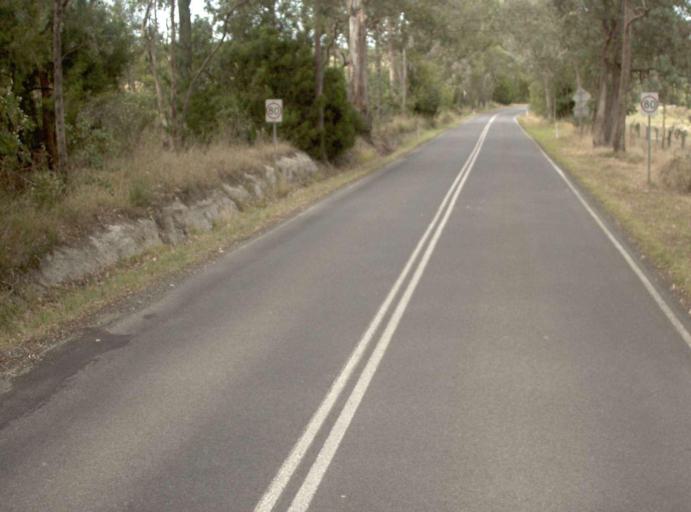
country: AU
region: Victoria
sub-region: Latrobe
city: Traralgon
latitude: -38.1395
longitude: 146.4886
